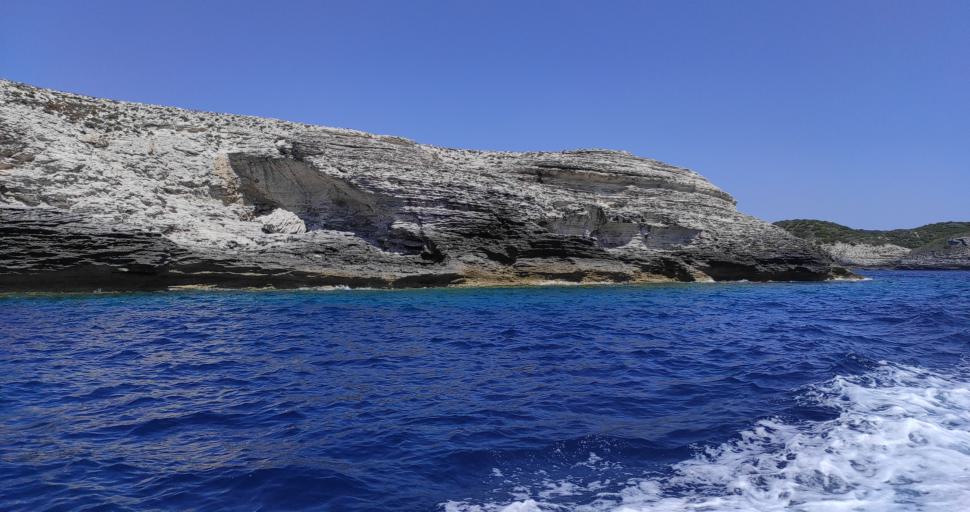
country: FR
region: Corsica
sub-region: Departement de la Corse-du-Sud
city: Bonifacio
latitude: 41.3928
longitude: 9.1286
